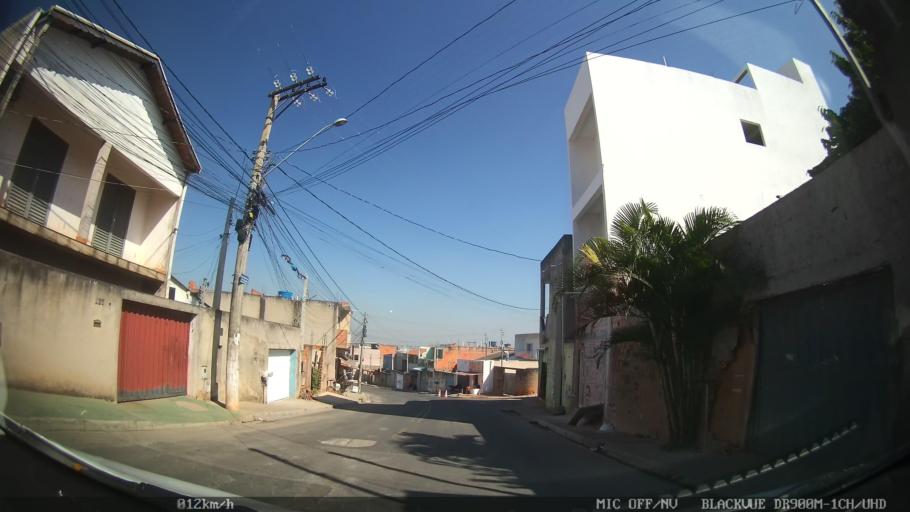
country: BR
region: Sao Paulo
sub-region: Campinas
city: Campinas
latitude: -22.9398
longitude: -47.0814
